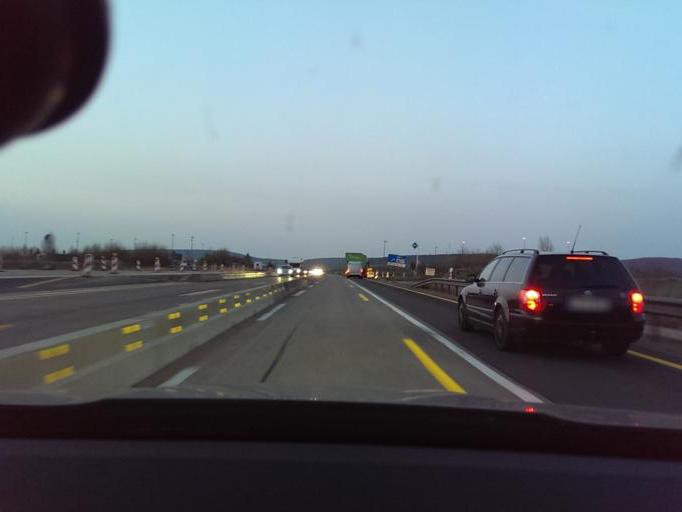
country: DE
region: Lower Saxony
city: Seesen
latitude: 51.9237
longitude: 10.1403
